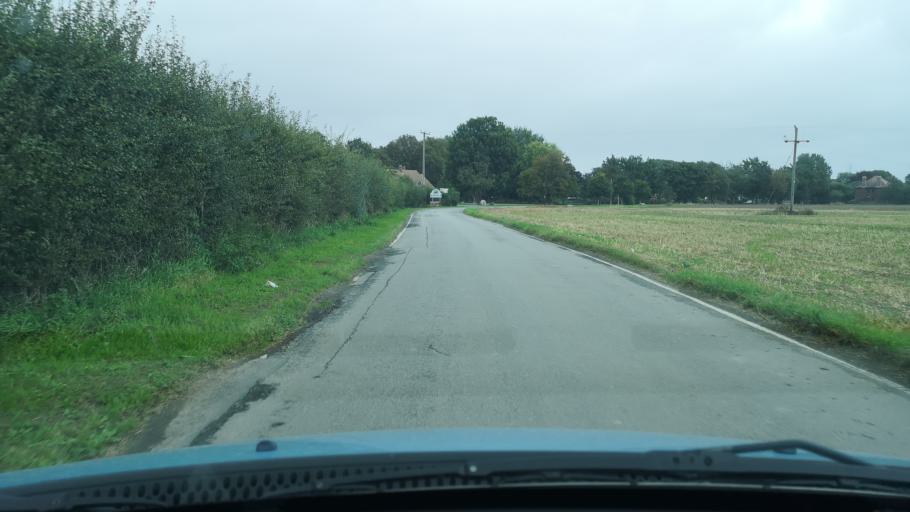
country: GB
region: England
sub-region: North Lincolnshire
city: Burton upon Stather
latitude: 53.6583
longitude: -0.7240
